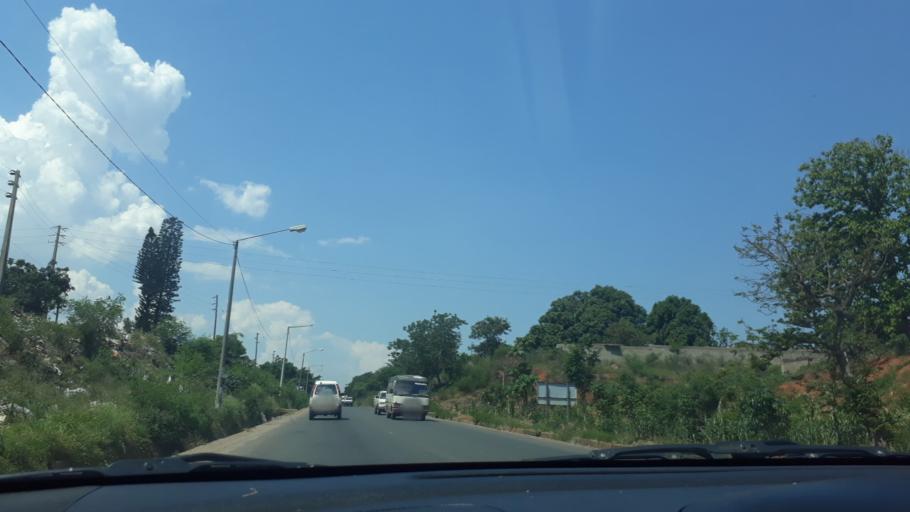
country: MZ
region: Maputo
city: Matola
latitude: -25.9632
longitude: 32.4475
